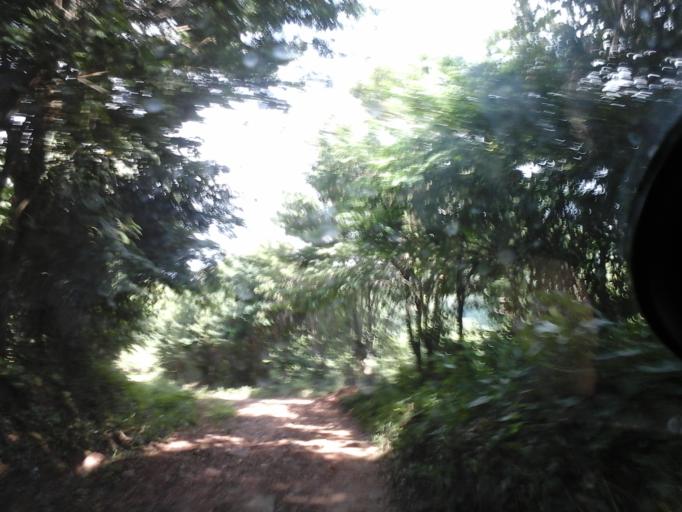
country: CO
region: Cesar
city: San Diego
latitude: 10.2734
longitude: -73.0941
